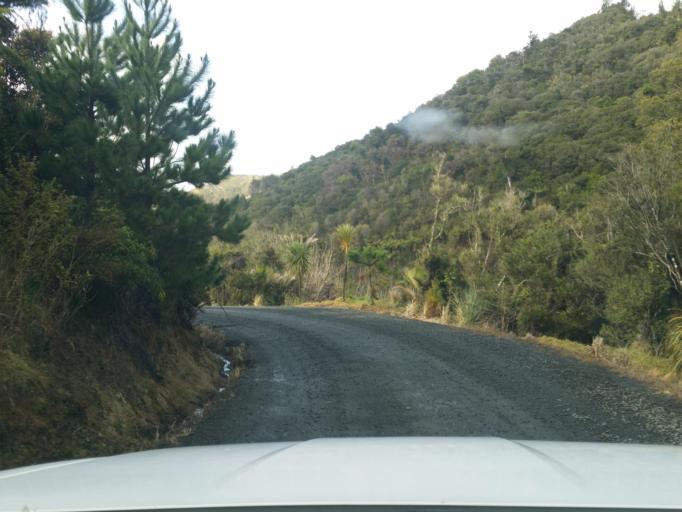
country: NZ
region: Northland
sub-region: Kaipara District
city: Dargaville
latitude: -35.7833
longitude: 173.7698
